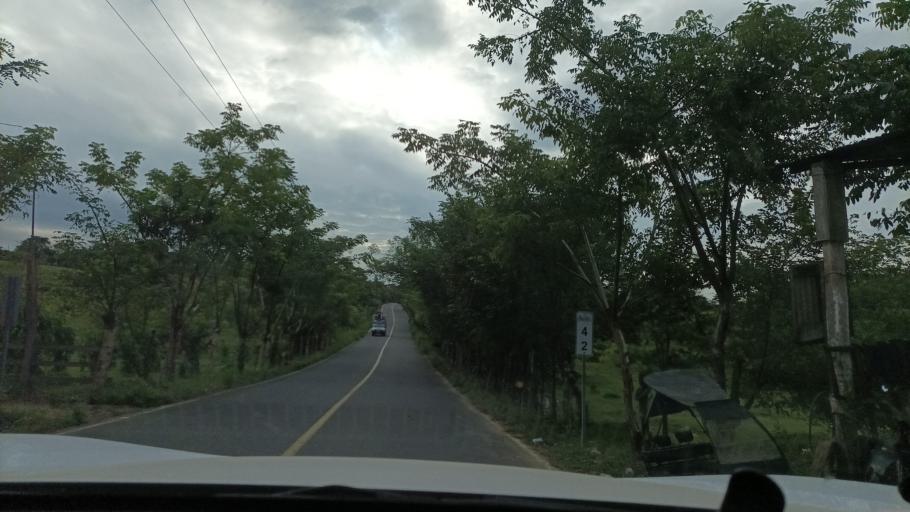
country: MX
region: Veracruz
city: Hidalgotitlan
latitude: 17.7162
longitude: -94.4748
